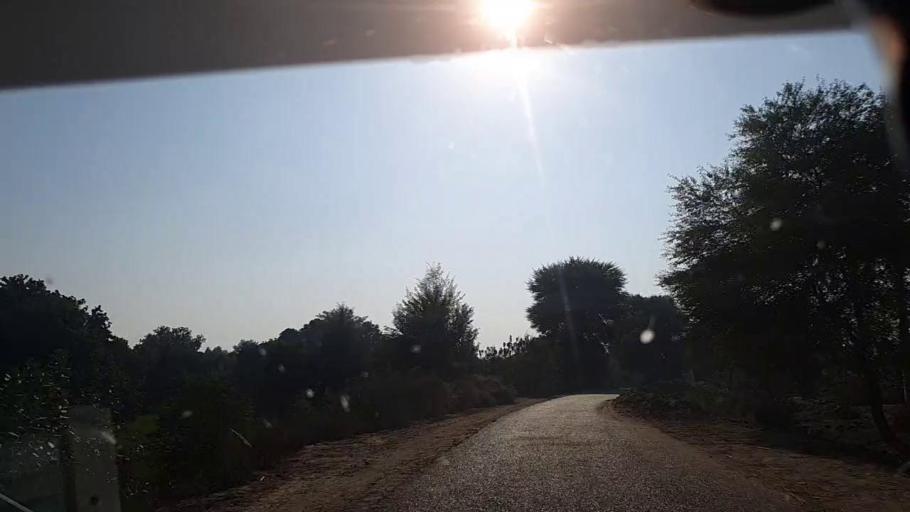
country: PK
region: Sindh
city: Sobhadero
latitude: 27.2362
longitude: 68.2790
